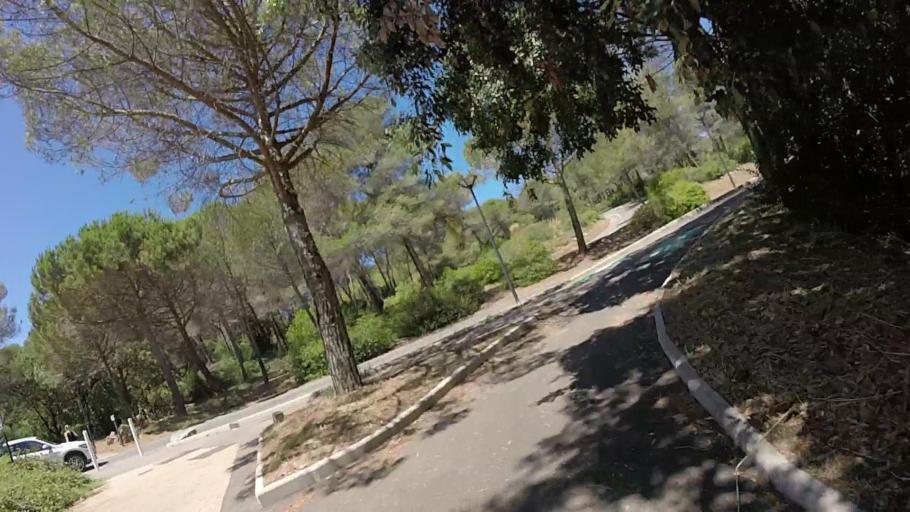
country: FR
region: Provence-Alpes-Cote d'Azur
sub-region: Departement des Alpes-Maritimes
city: Valbonne
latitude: 43.6248
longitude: 7.0373
